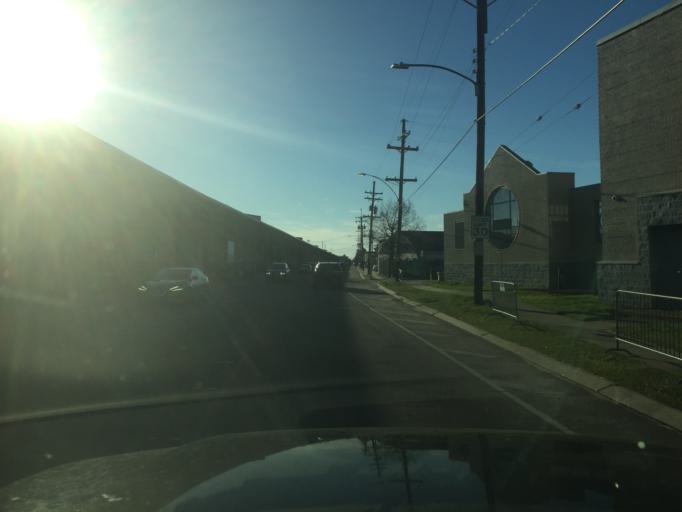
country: US
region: Louisiana
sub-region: Jefferson Parish
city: Harvey
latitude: 29.9183
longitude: -90.0877
